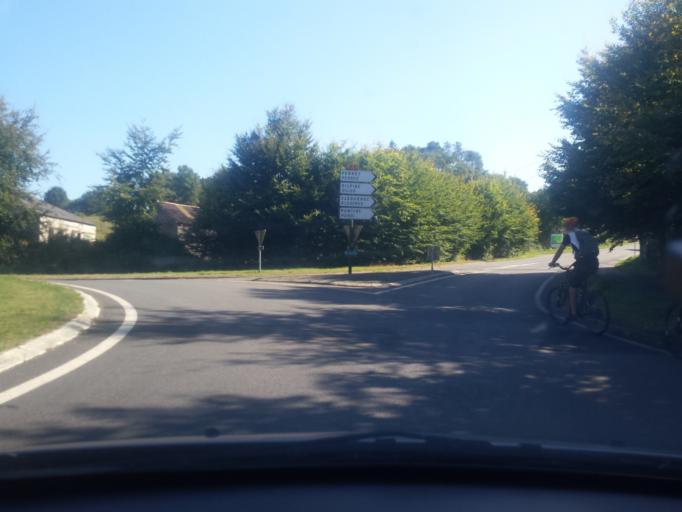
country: FR
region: Brittany
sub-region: Departement des Cotes-d'Armor
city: Gouarec
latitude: 48.2236
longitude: -3.1766
